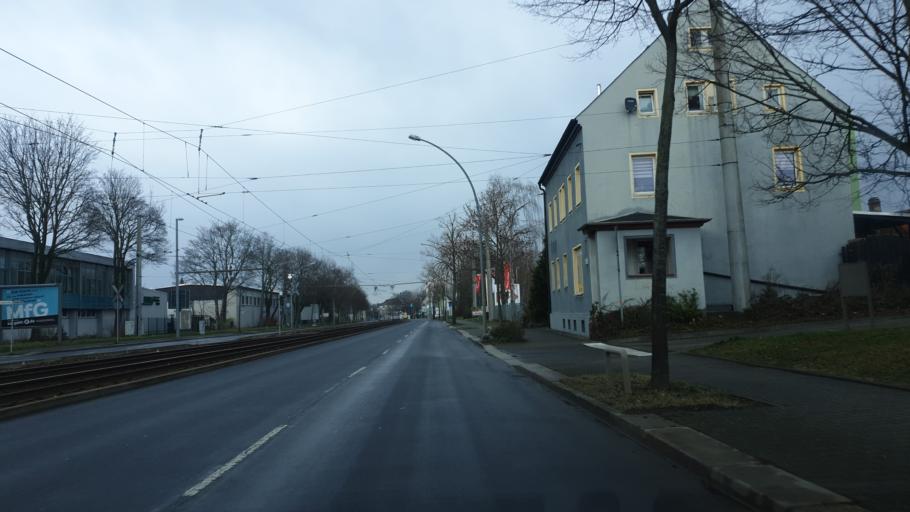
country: DE
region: Saxony
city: Chemnitz
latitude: 50.8034
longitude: 12.9117
